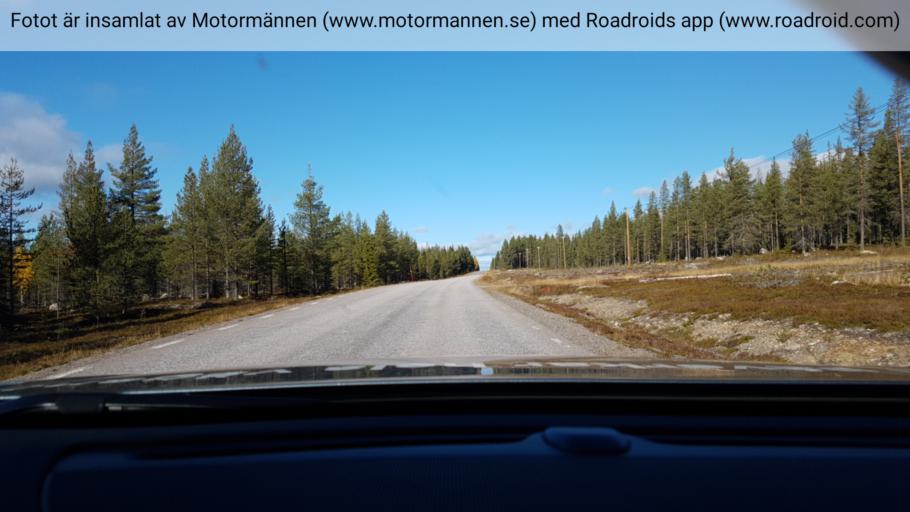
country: SE
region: Vaesterbotten
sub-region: Mala Kommun
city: Mala
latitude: 65.7828
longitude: 18.5004
